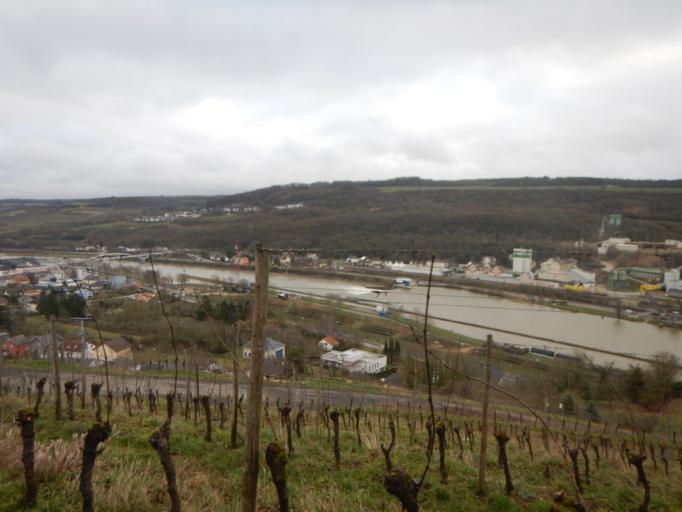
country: DE
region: Rheinland-Pfalz
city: Wellen
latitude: 49.6735
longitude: 6.4319
